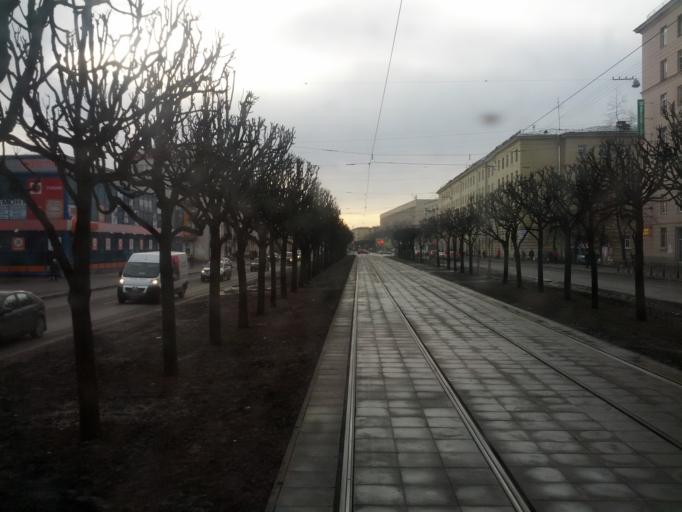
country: RU
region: St.-Petersburg
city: Centralniy
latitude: 59.9265
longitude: 30.4143
